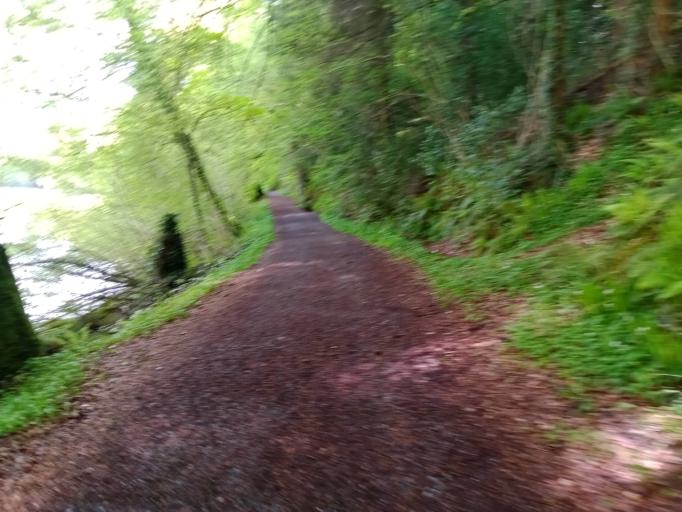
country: IE
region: Leinster
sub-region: Kilkenny
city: Thomastown
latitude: 52.4822
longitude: -7.0604
